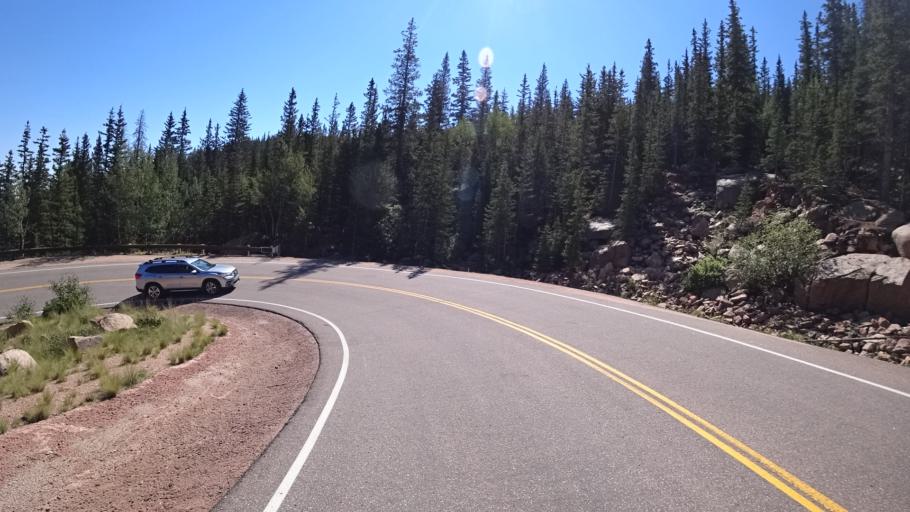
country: US
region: Colorado
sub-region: El Paso County
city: Cascade-Chipita Park
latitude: 38.8909
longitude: -105.0670
